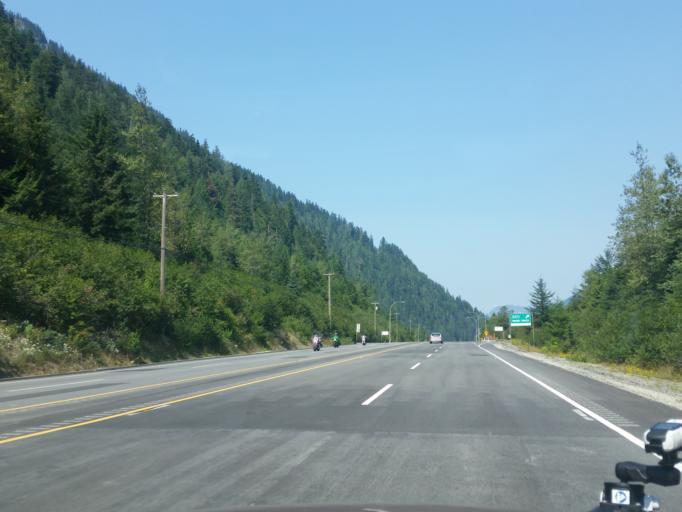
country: CA
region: British Columbia
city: Hope
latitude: 49.2961
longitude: -121.2622
